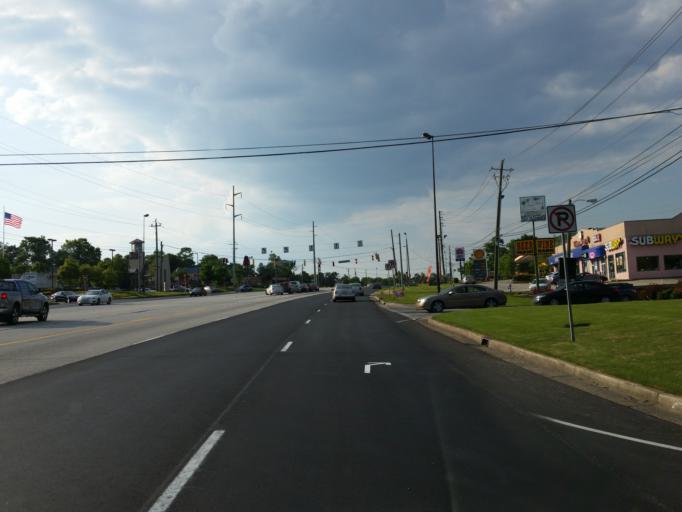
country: US
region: Georgia
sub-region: Cobb County
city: Vinings
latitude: 33.8274
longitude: -84.4914
